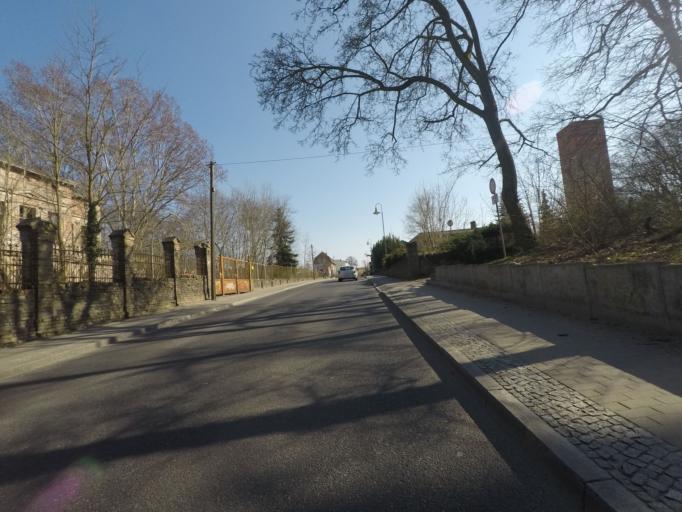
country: DE
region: Brandenburg
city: Eberswalde
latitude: 52.8370
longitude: 13.7952
